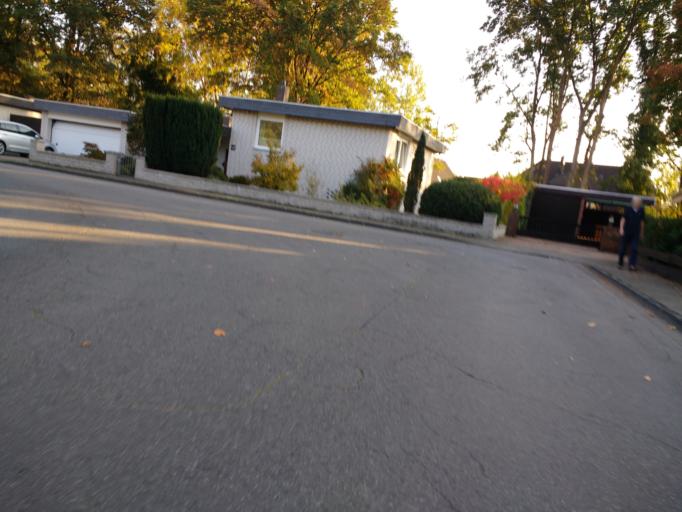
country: DE
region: Lower Saxony
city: Gifhorn
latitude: 52.4676
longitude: 10.5566
